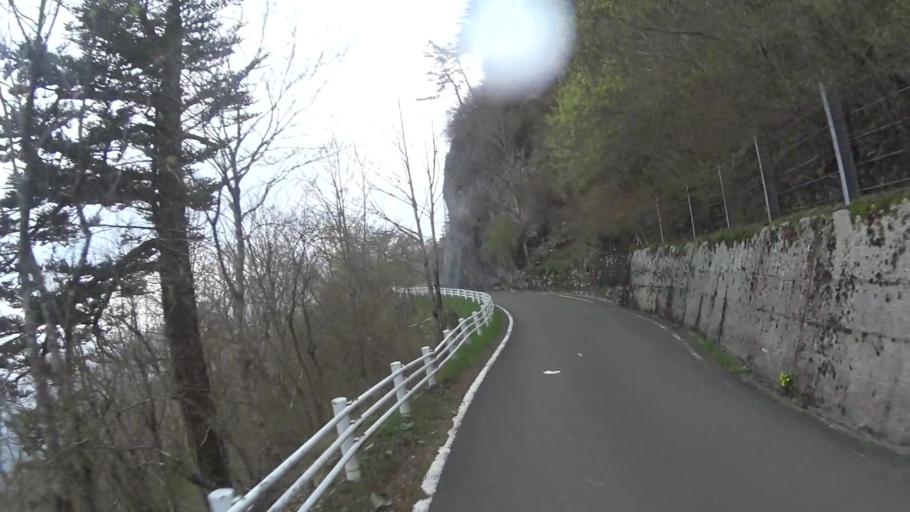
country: JP
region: Ehime
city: Saijo
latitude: 33.7803
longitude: 133.2382
